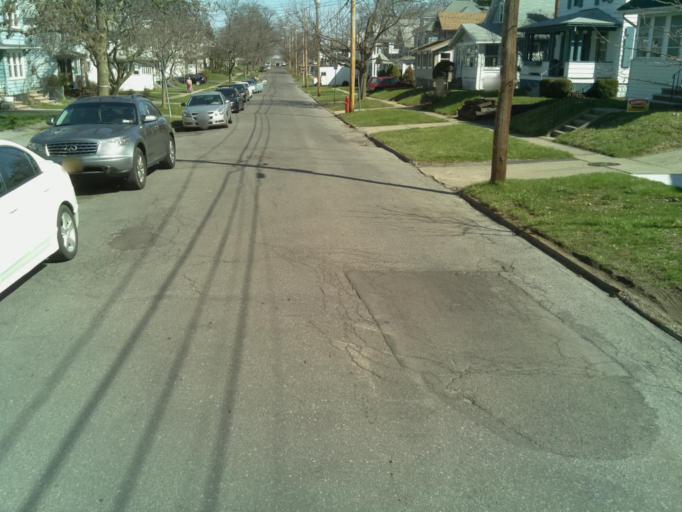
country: US
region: New York
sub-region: Onondaga County
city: Lyncourt
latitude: 43.0698
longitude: -76.1042
